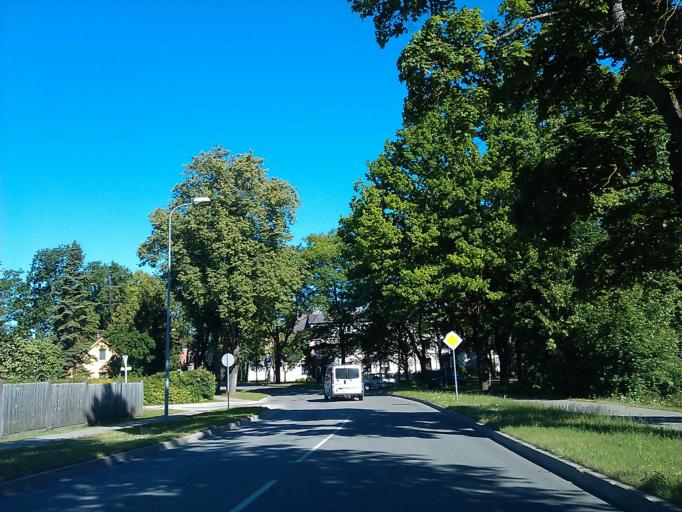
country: LV
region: Cesu Rajons
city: Cesis
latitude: 57.3084
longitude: 25.2510
